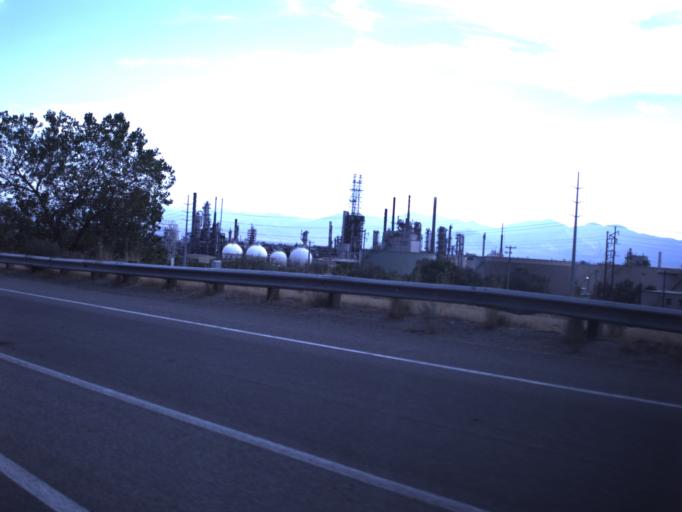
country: US
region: Utah
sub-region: Davis County
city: North Salt Lake
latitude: 40.8305
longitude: -111.9173
